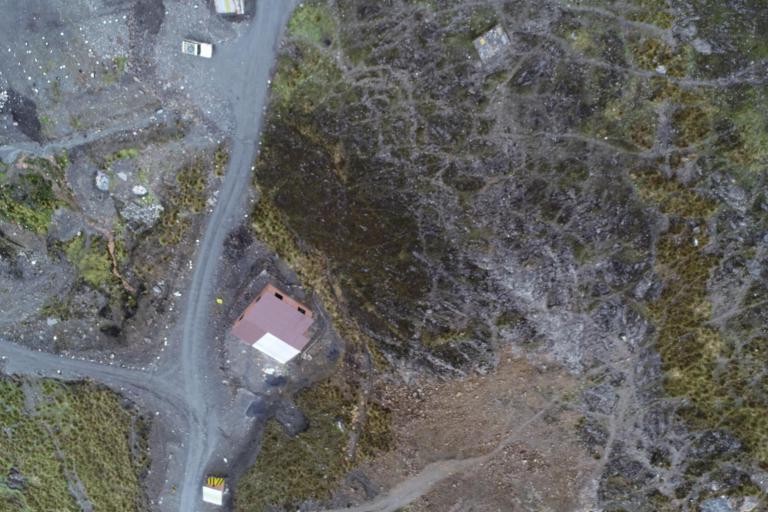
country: BO
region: La Paz
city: Sorata
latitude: -15.6629
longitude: -68.5120
